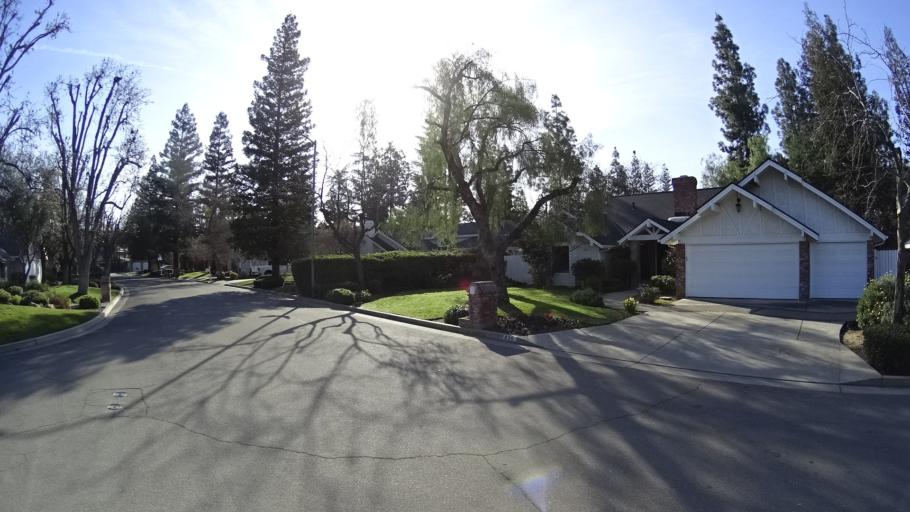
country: US
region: California
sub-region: Fresno County
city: Clovis
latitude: 36.8671
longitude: -119.7681
